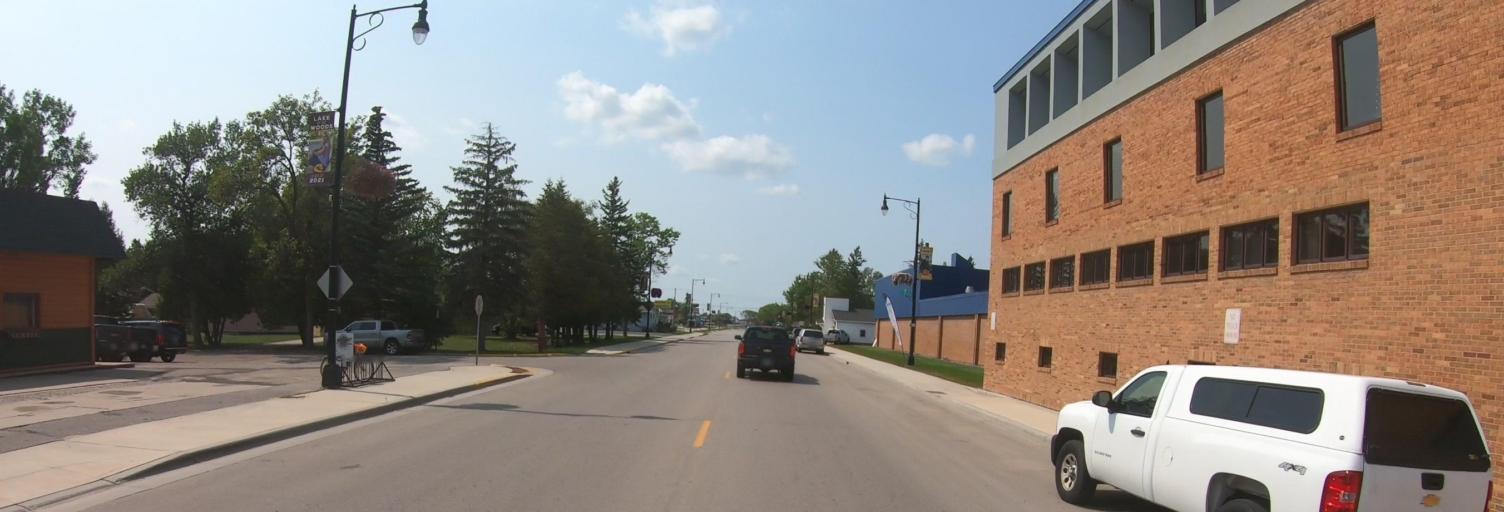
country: US
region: Minnesota
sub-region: Lake of the Woods County
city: Baudette
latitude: 48.7129
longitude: -94.6016
